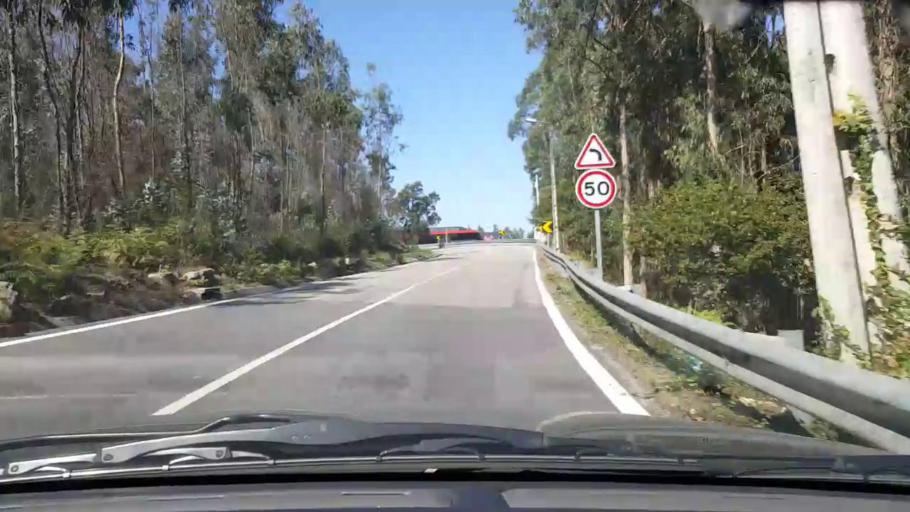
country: PT
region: Porto
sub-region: Vila do Conde
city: Arvore
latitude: 41.3422
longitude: -8.6558
